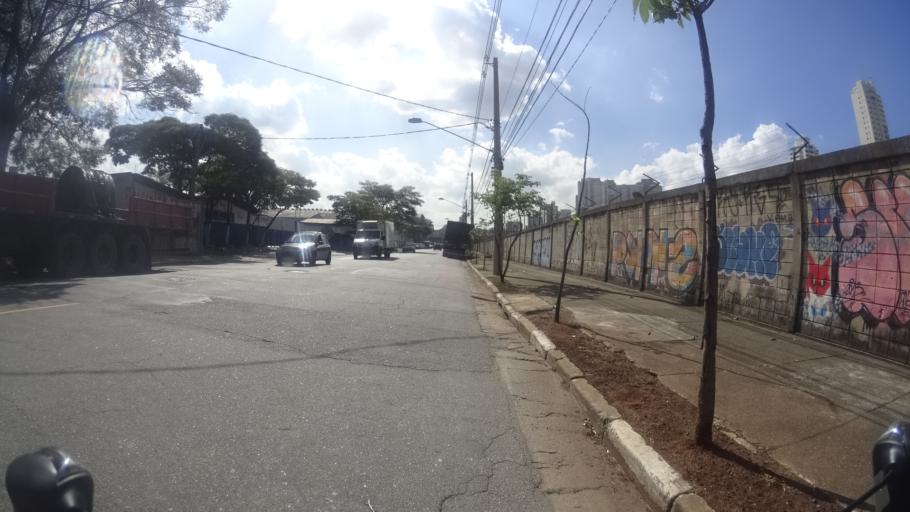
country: BR
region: Sao Paulo
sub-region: Sao Paulo
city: Sao Paulo
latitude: -23.5742
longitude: -46.5947
